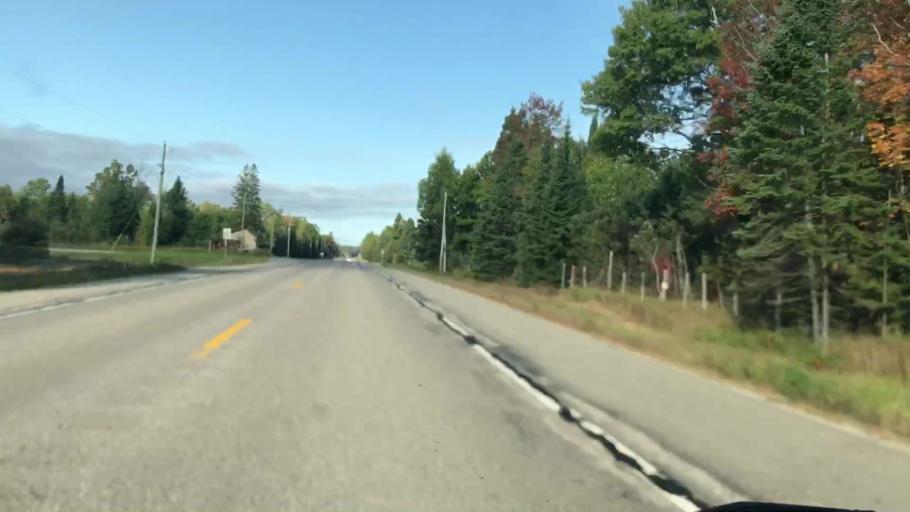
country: US
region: Michigan
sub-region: Luce County
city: Newberry
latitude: 46.3034
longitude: -85.3618
